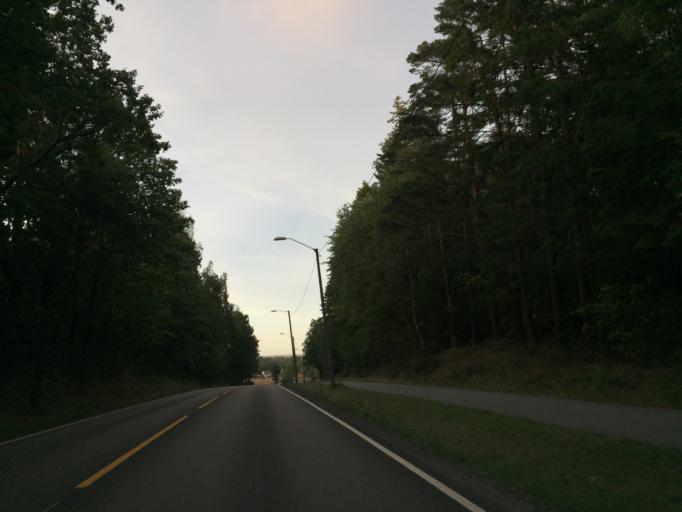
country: NO
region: Ostfold
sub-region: Fredrikstad
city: Fredrikstad
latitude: 59.1865
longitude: 10.9306
